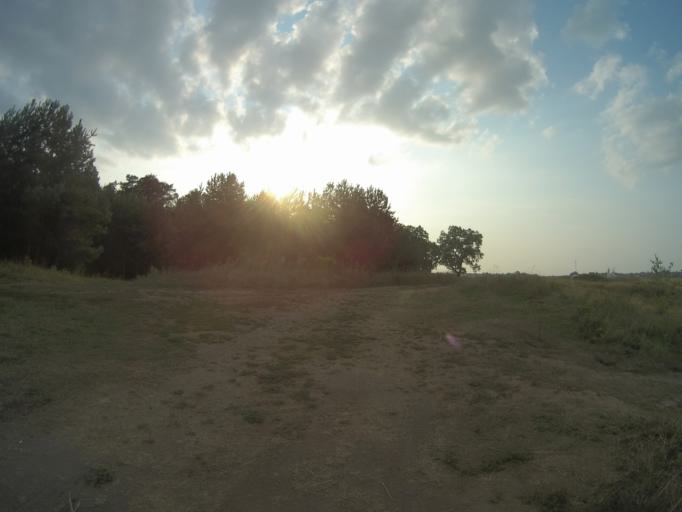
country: RU
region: Vladimir
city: Orgtrud
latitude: 56.2970
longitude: 40.6161
